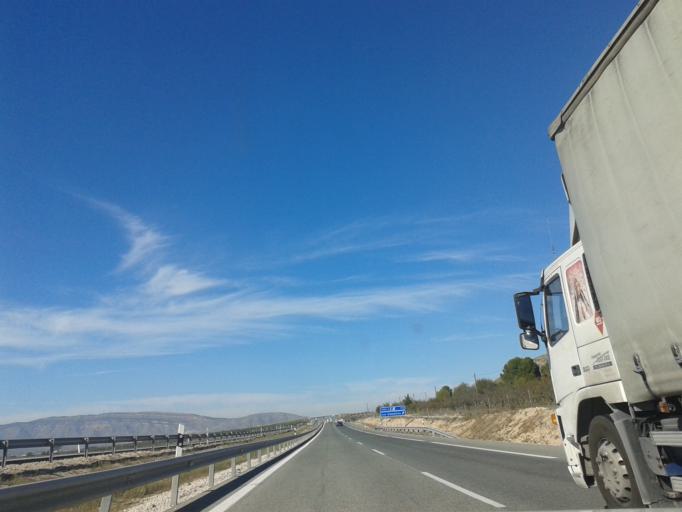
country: ES
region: Valencia
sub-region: Provincia de Alicante
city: Villena
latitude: 38.6878
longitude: -0.9062
